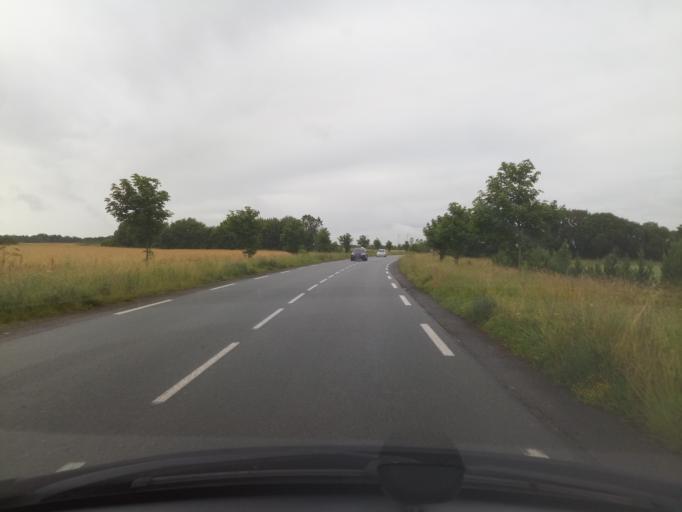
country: FR
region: Poitou-Charentes
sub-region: Departement de la Charente-Maritime
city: Courcon
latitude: 46.1860
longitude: -0.8544
